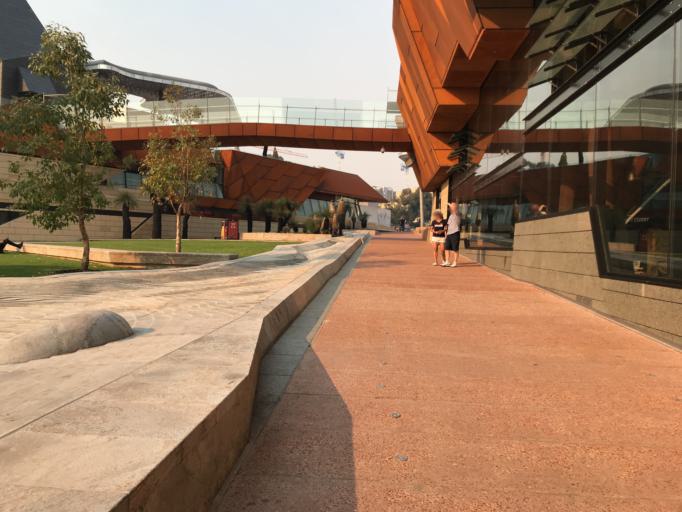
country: AU
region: Western Australia
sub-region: Cambridge
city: Perth
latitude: -31.9506
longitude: 115.8583
